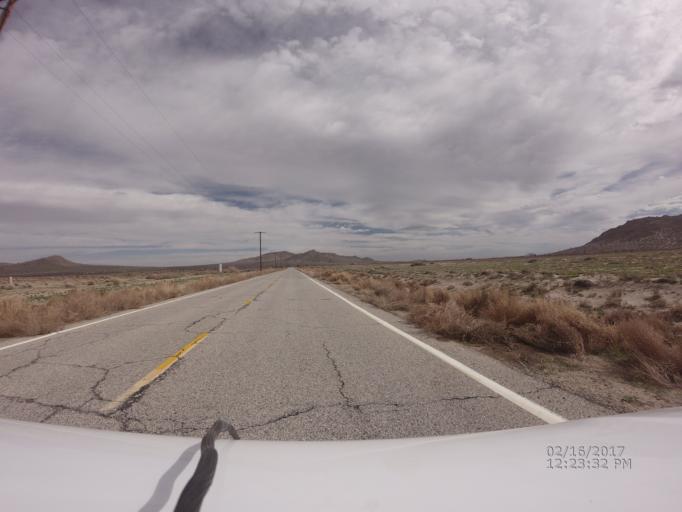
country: US
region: California
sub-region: Los Angeles County
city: Lake Los Angeles
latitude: 34.6754
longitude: -117.8594
